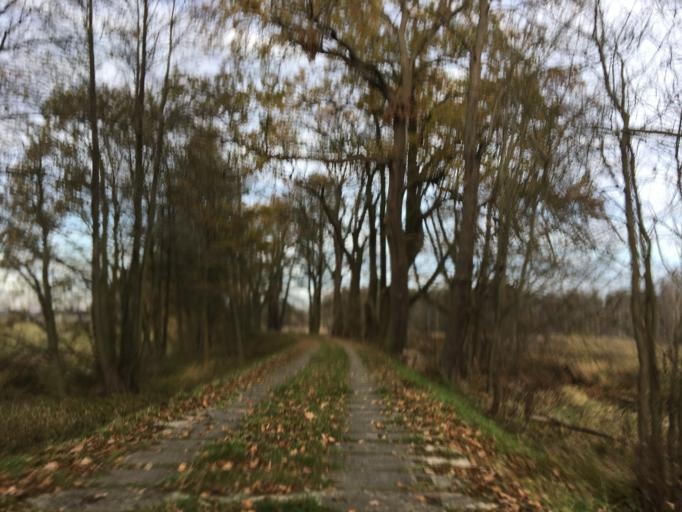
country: DE
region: Brandenburg
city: Schlepzig
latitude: 52.0224
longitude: 13.8584
